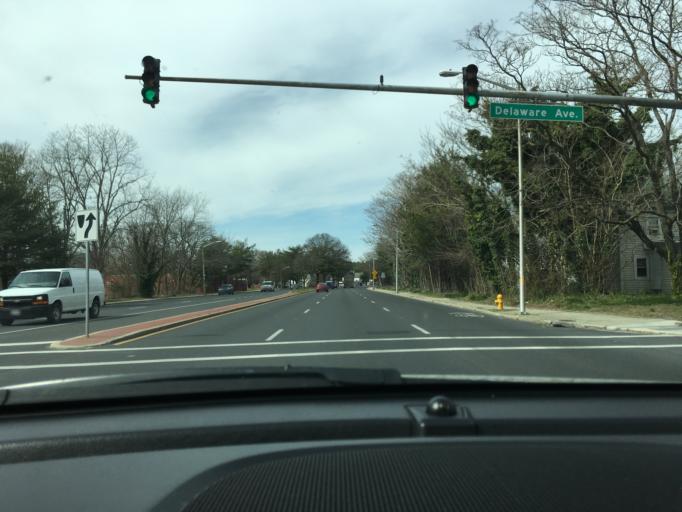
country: US
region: Maryland
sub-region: Wicomico County
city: Salisbury
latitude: 38.3679
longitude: -75.6100
